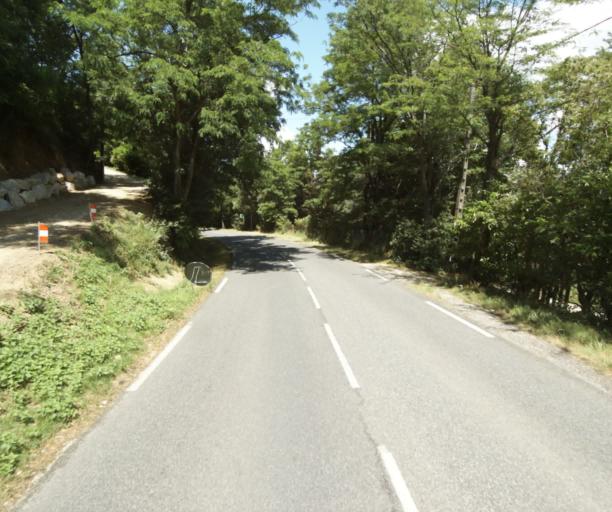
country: FR
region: Midi-Pyrenees
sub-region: Departement de la Haute-Garonne
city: Revel
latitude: 43.4461
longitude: 2.0137
